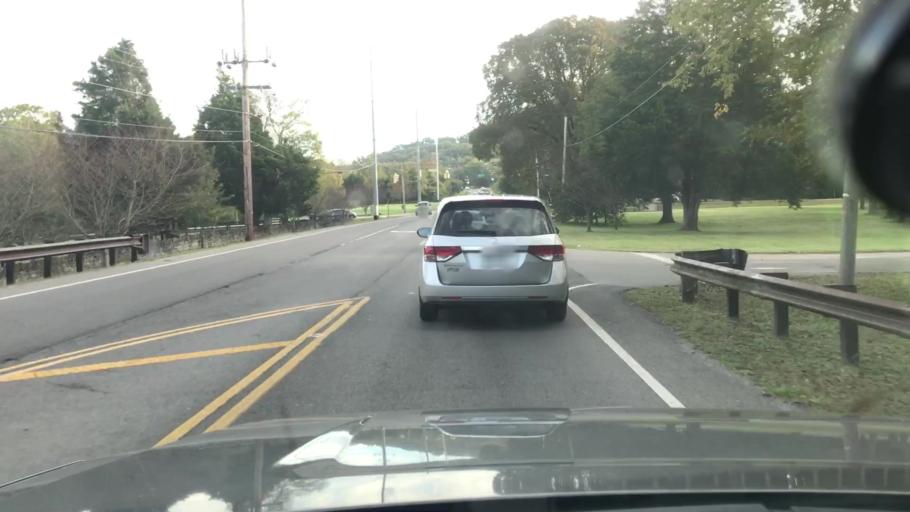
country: US
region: Tennessee
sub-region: Davidson County
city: Forest Hills
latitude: 36.0778
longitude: -86.8379
